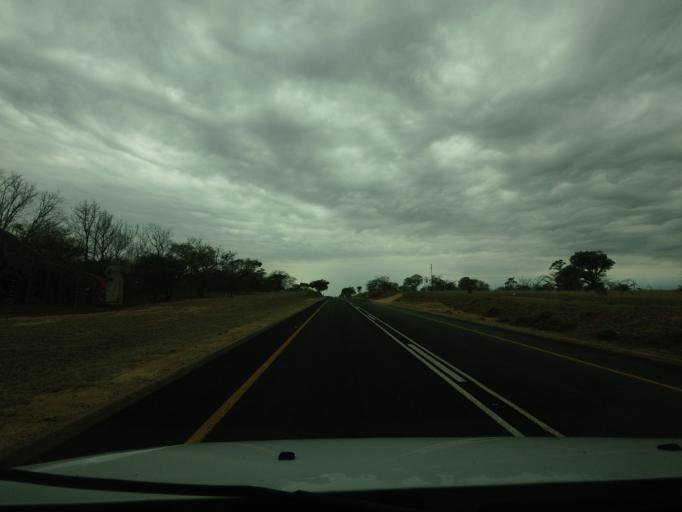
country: ZA
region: Limpopo
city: Thulamahashi
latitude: -24.5661
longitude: 31.1084
